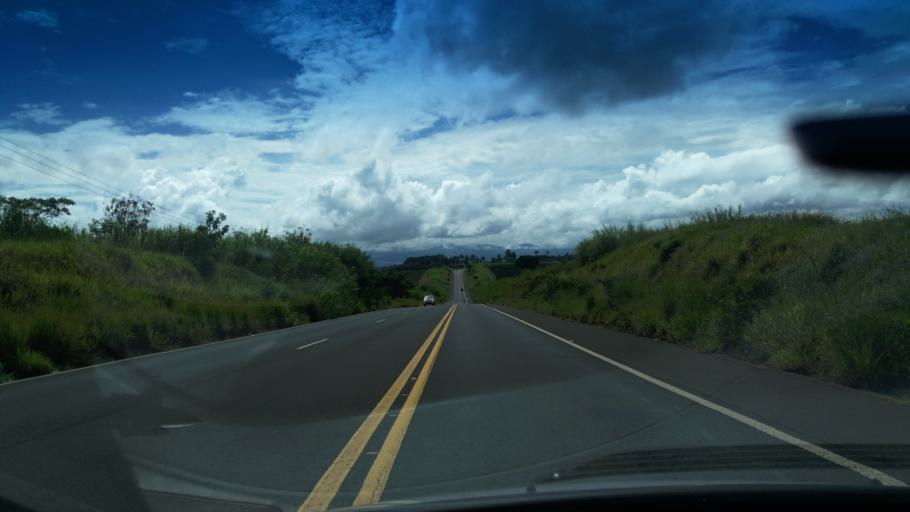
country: BR
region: Sao Paulo
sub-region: Santo Antonio Do Jardim
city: Espirito Santo do Pinhal
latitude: -22.1479
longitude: -46.7181
